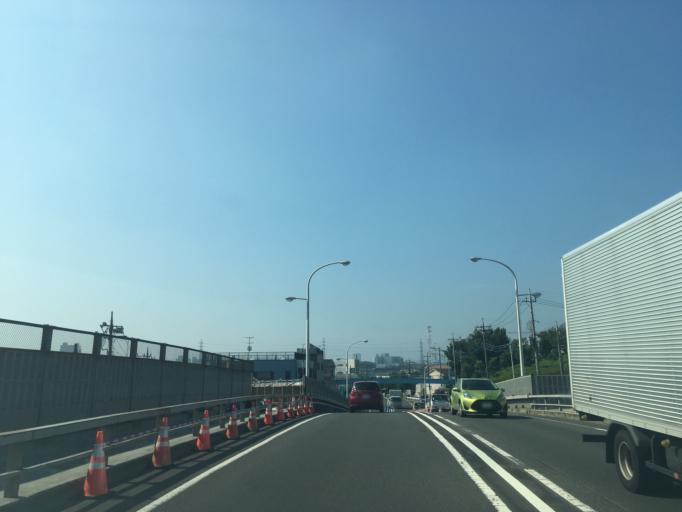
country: JP
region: Tokyo
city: Hino
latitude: 35.6840
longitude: 139.3698
